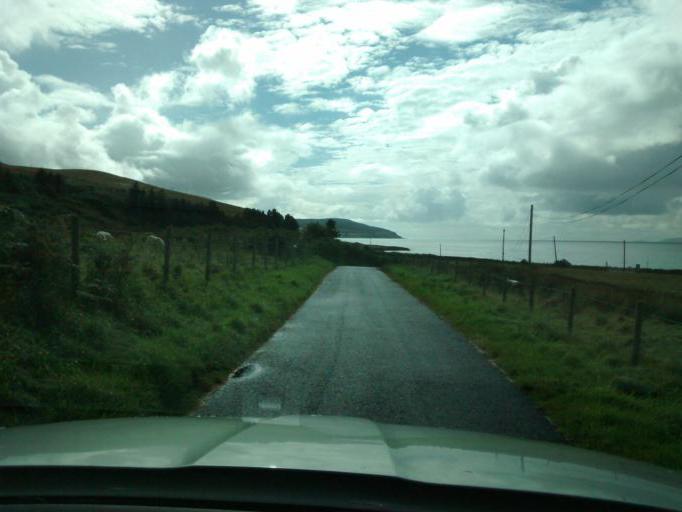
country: GB
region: Scotland
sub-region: North Ayrshire
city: Isle of Arran
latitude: 55.5728
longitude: -5.3480
